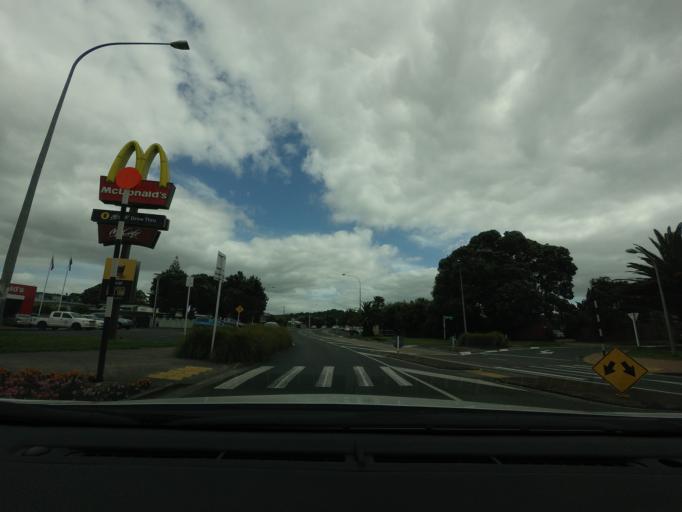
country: NZ
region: Auckland
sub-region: Auckland
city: Rothesay Bay
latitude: -36.5850
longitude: 174.6950
